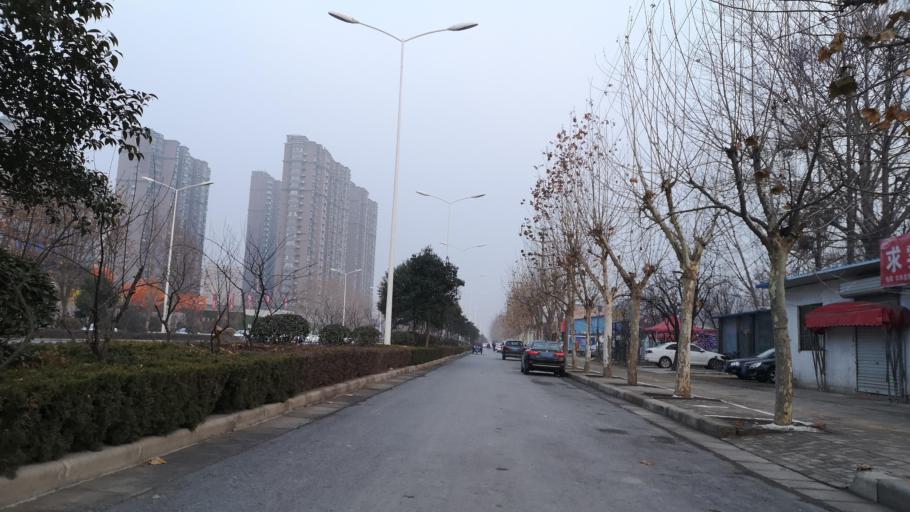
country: CN
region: Henan Sheng
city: Zhongyuanlu
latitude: 35.7475
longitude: 115.0567
